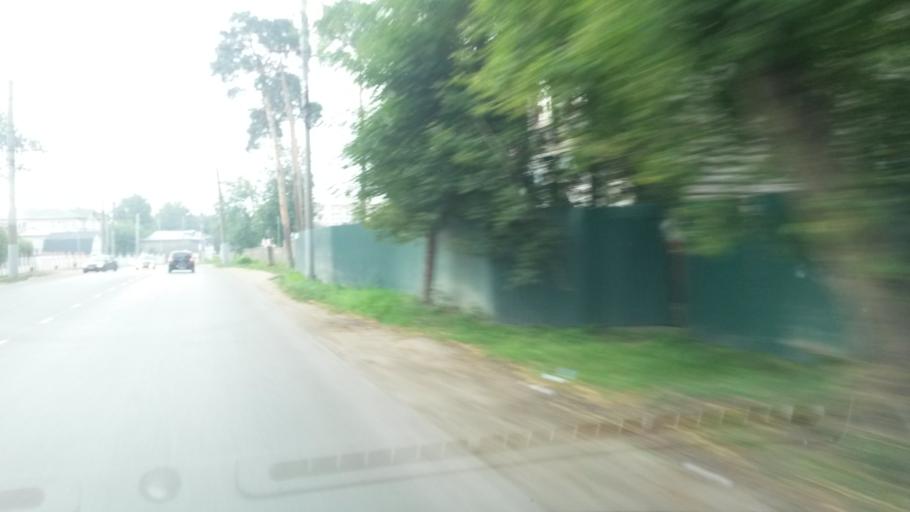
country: RU
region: Ivanovo
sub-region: Gorod Ivanovo
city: Ivanovo
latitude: 57.0223
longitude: 40.9475
